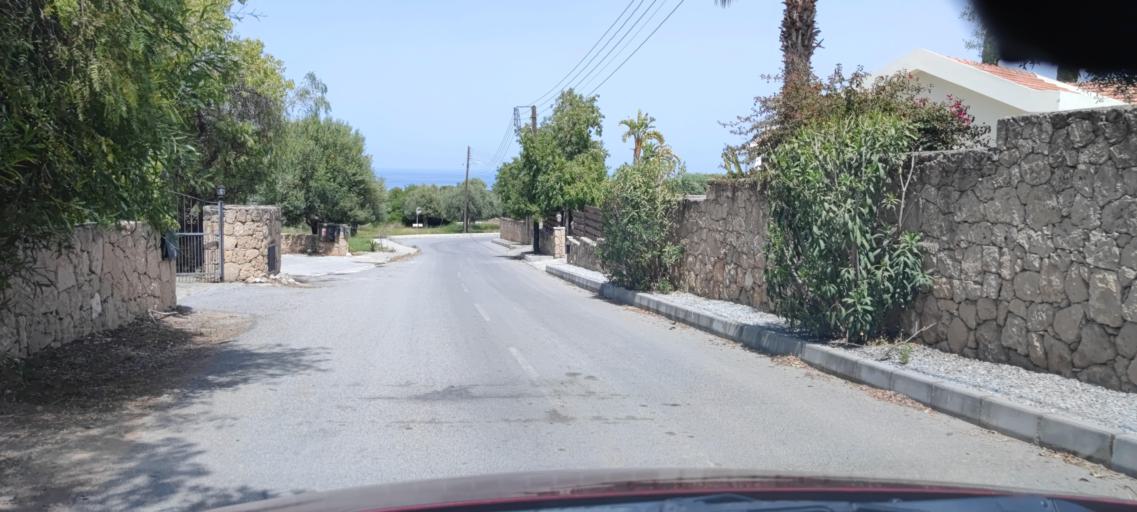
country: CY
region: Keryneia
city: Kyrenia
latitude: 35.3141
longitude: 33.3615
